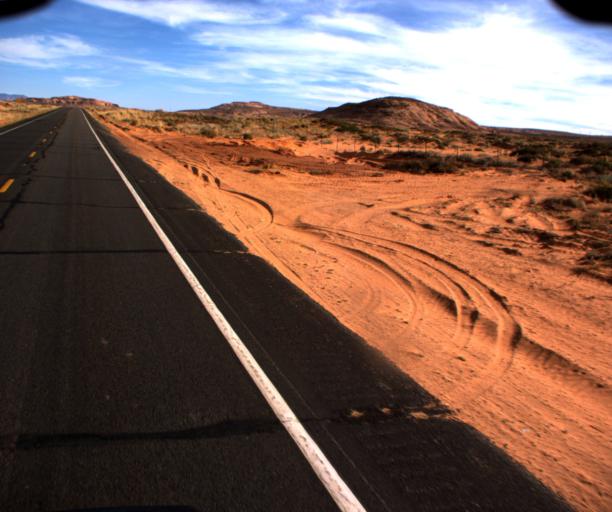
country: US
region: Arizona
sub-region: Apache County
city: Many Farms
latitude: 36.9352
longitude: -109.6327
